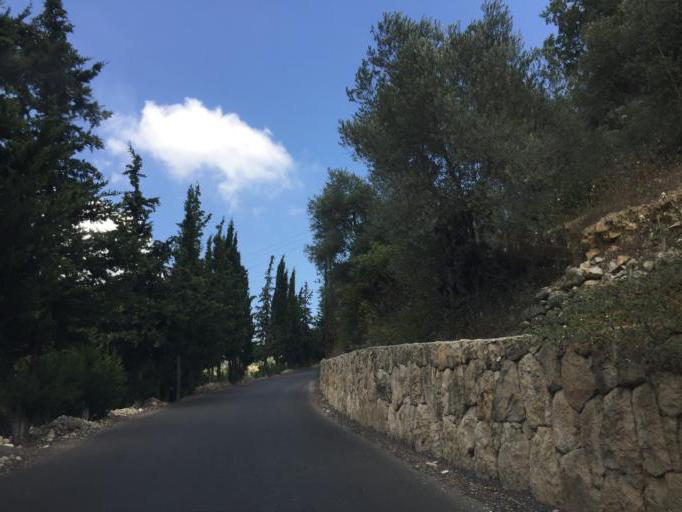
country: LB
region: Mont-Liban
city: Beit ed Dine
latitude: 33.6953
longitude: 35.5785
